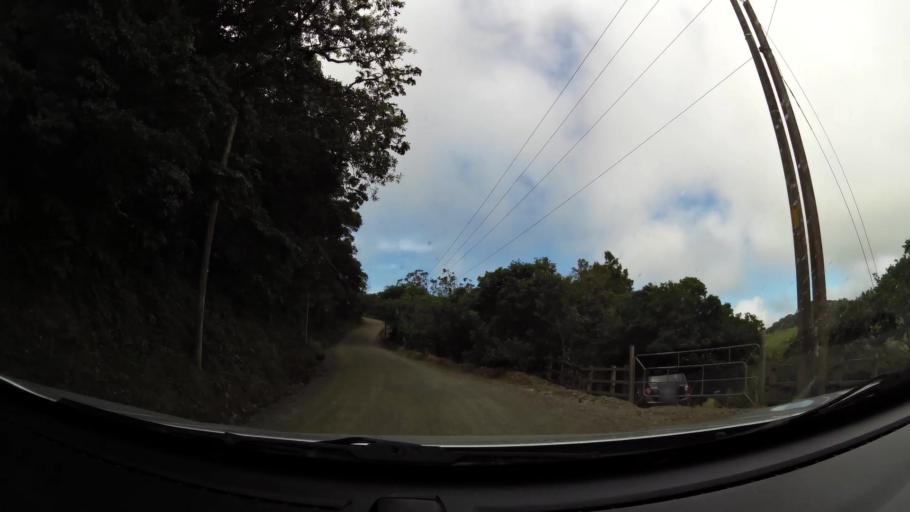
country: CR
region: Guanacaste
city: Juntas
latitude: 10.3511
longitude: -84.9085
